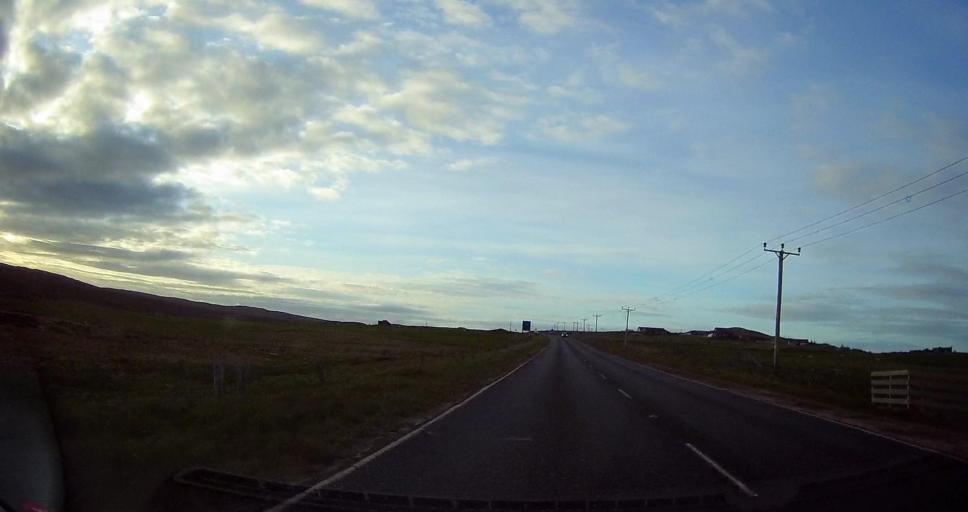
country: GB
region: Scotland
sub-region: Shetland Islands
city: Lerwick
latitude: 60.1949
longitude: -1.2321
